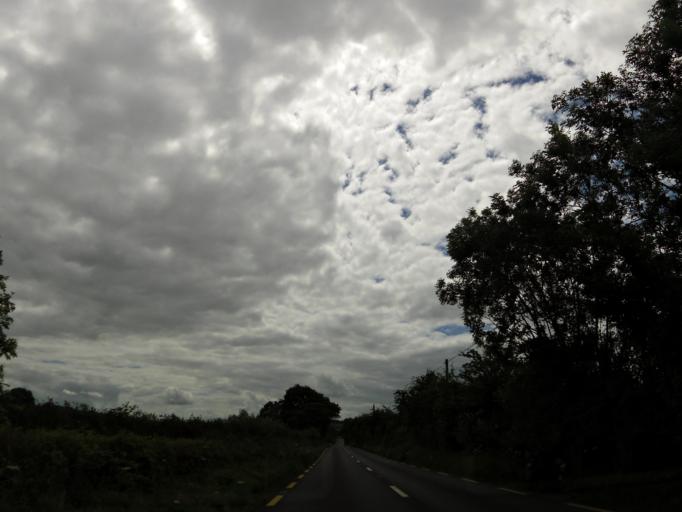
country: IE
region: Munster
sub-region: North Tipperary
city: Nenagh
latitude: 52.7798
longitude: -8.0313
